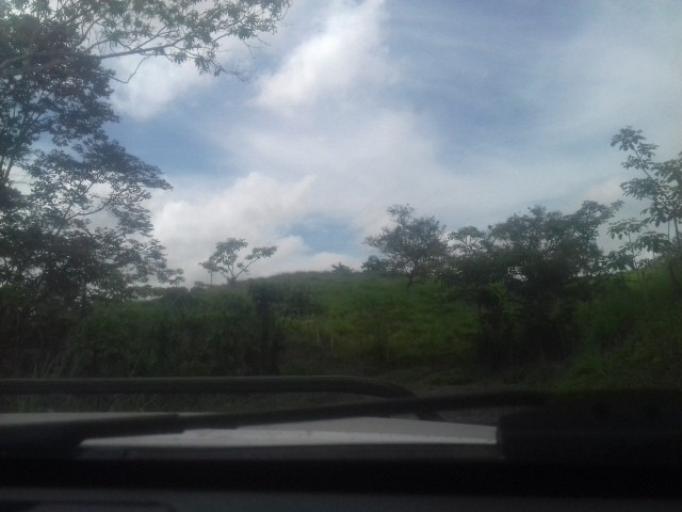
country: NI
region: Atlantico Norte (RAAN)
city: Waslala
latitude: 13.4945
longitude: -85.2302
